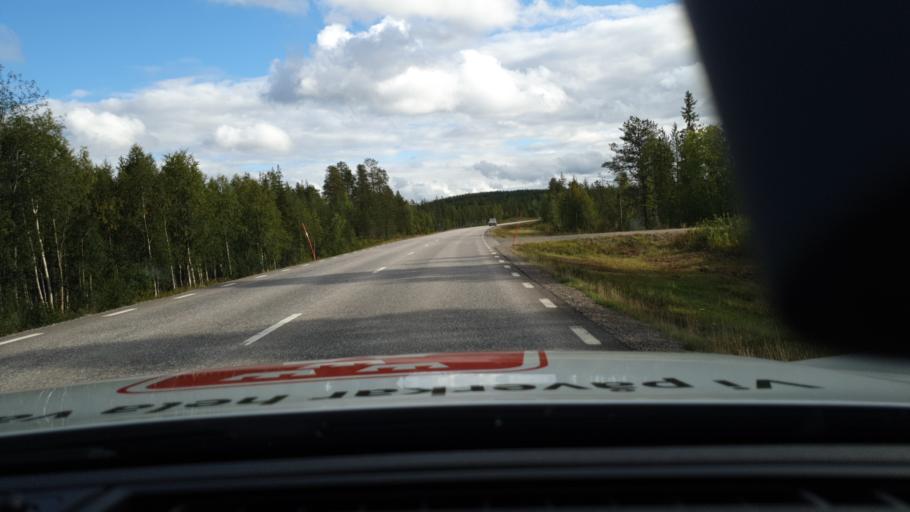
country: SE
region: Norrbotten
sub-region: Gallivare Kommun
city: Gaellivare
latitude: 67.0389
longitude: 21.2321
